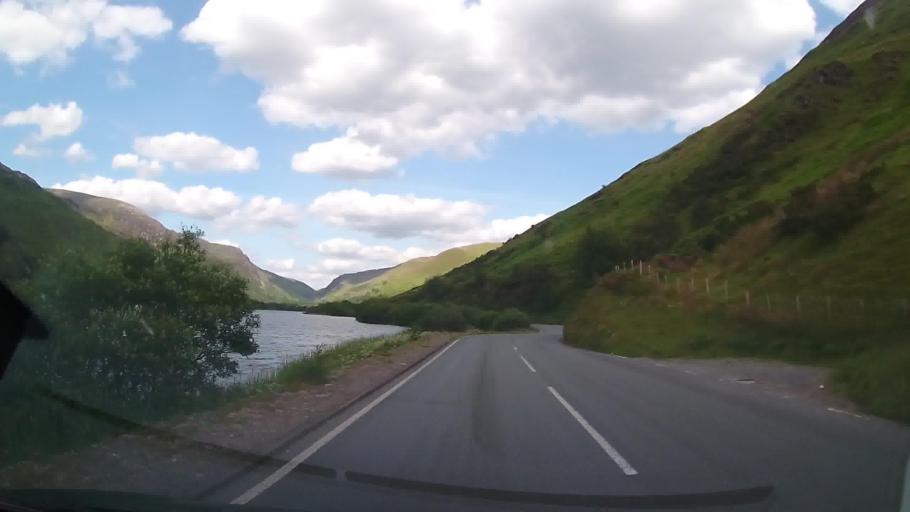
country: GB
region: Wales
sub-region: Gwynedd
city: Corris
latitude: 52.6685
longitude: -3.9010
